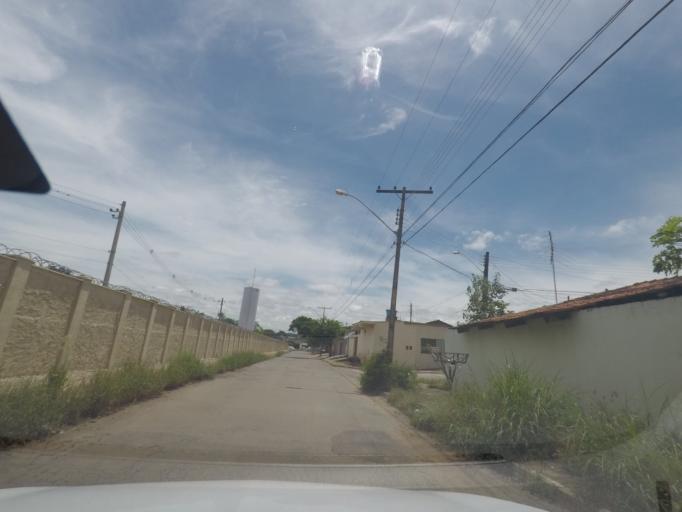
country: BR
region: Goias
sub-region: Goiania
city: Goiania
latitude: -16.6597
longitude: -49.1983
